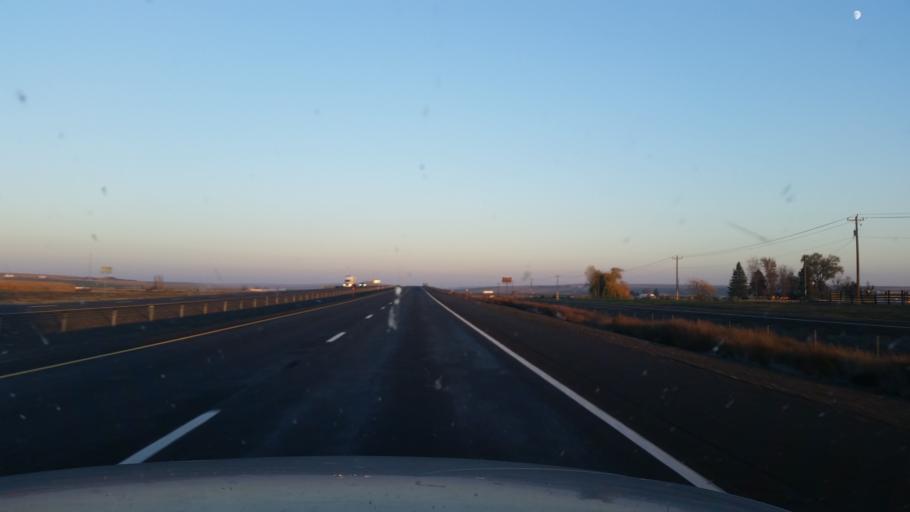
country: US
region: Washington
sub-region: Grant County
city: Warden
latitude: 47.0860
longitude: -119.0609
